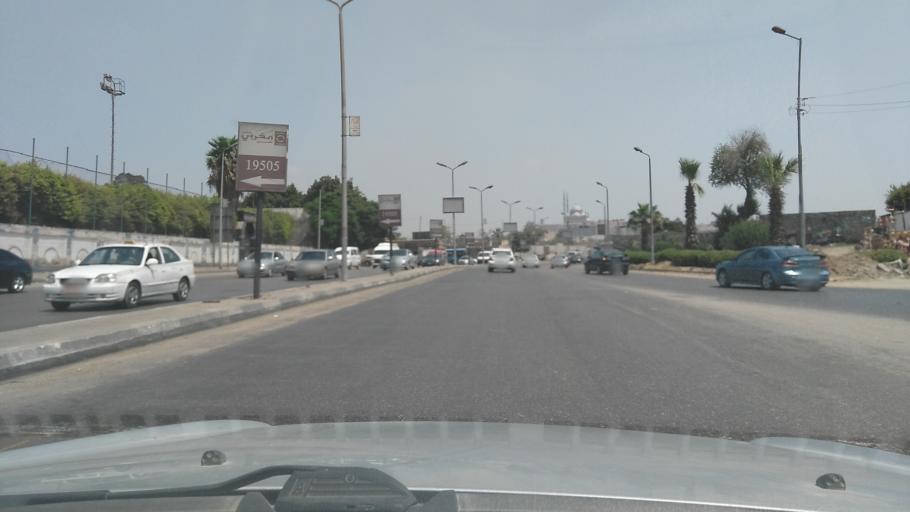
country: EG
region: Al Jizah
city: Al Jizah
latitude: 30.0162
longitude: 31.2503
